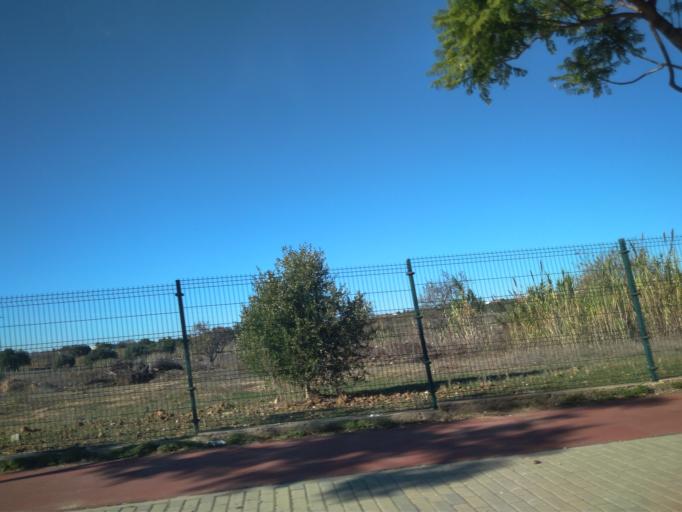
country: PT
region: Faro
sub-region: Albufeira
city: Ferreiras
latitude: 37.1097
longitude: -8.2303
